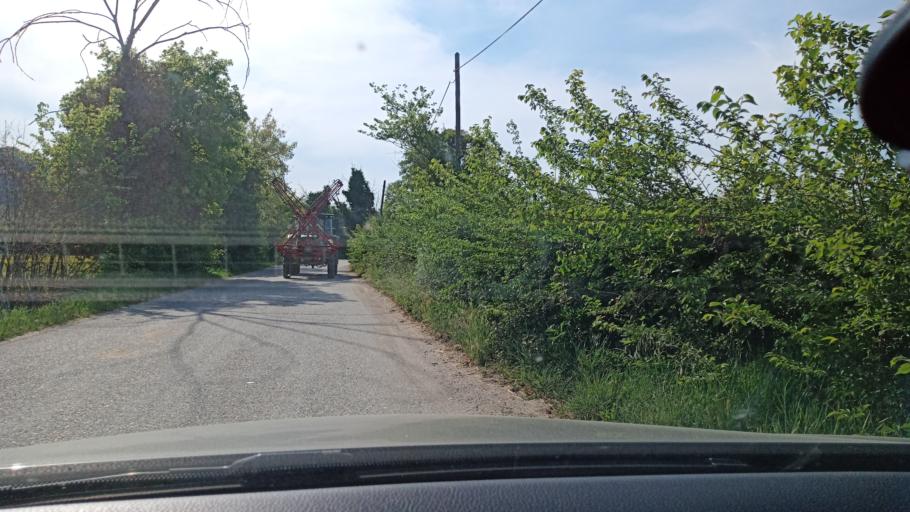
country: IT
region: Latium
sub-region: Citta metropolitana di Roma Capitale
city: Ponzano Romano
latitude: 42.2674
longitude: 12.5572
